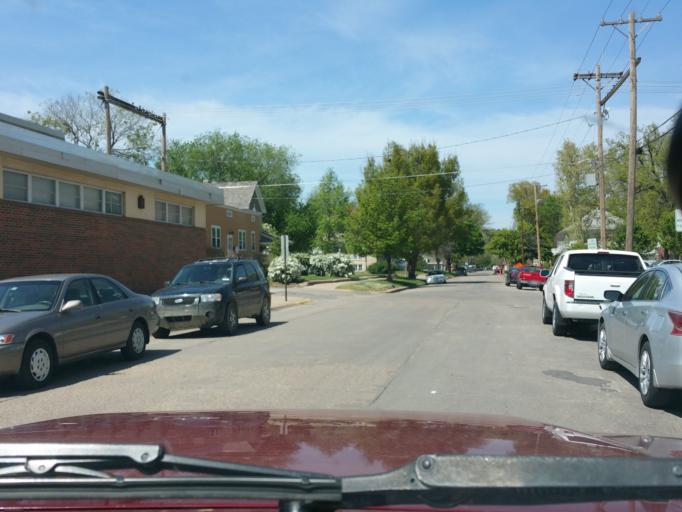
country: US
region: Kansas
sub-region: Riley County
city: Manhattan
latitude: 39.1816
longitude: -96.5634
